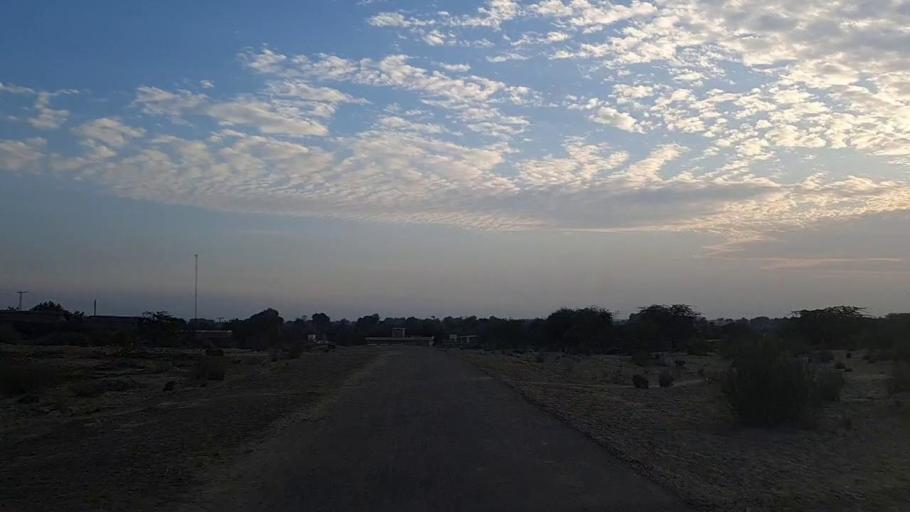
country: PK
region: Sindh
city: Daur
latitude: 26.4100
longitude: 68.4663
